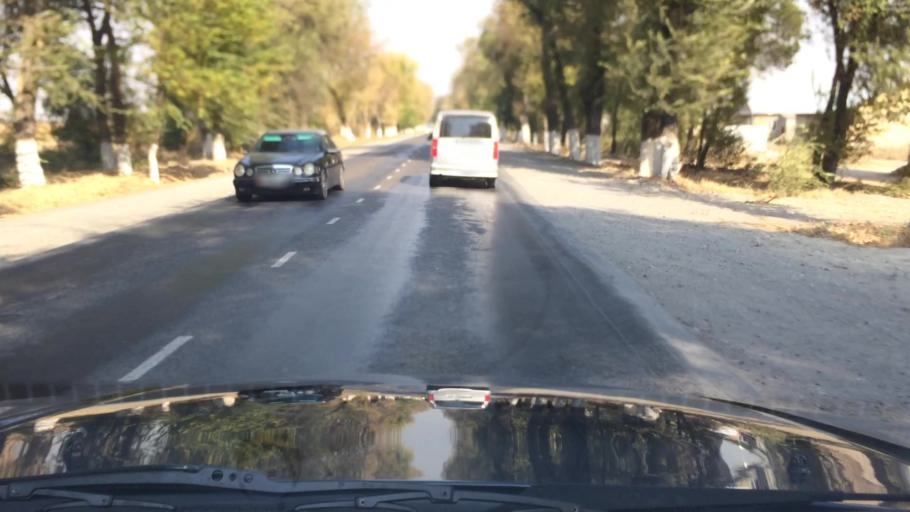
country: KG
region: Chuy
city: Lebedinovka
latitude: 42.9221
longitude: 74.6898
